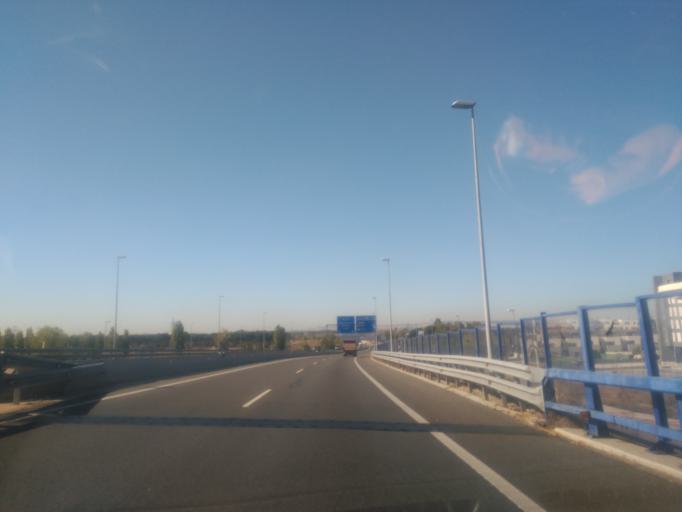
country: ES
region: Castille and Leon
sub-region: Provincia de Valladolid
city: Cisterniga
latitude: 41.6125
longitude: -4.7135
